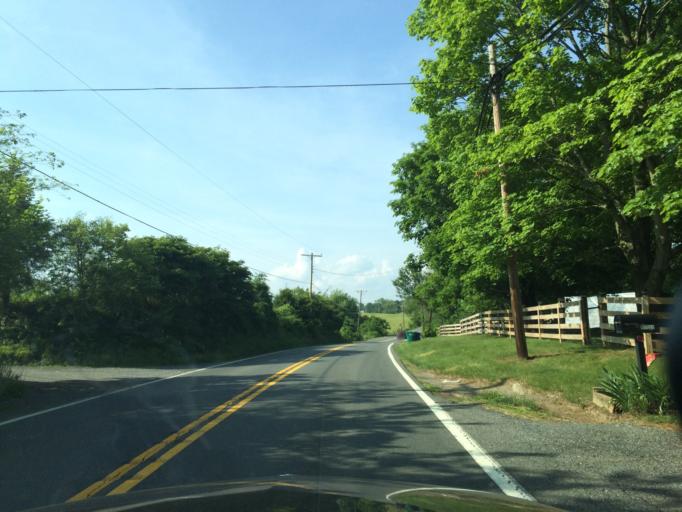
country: US
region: Maryland
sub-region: Montgomery County
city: Olney
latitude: 39.2164
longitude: -77.0614
